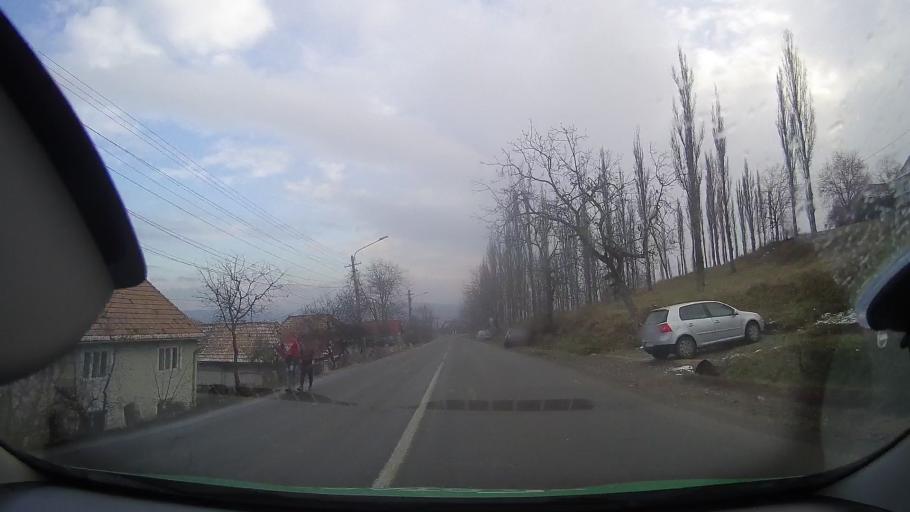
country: RO
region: Mures
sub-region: Municipiul Tarnaveni
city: Tarnaveni
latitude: 46.3386
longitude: 24.2796
